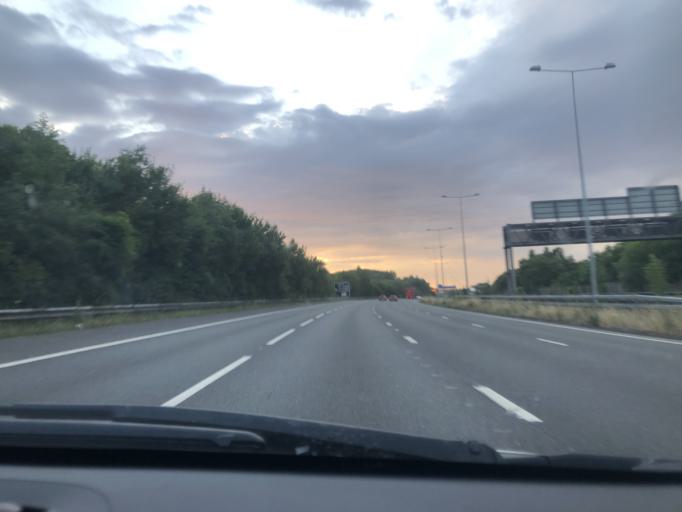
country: GB
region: England
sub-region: Medway
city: Cuxton
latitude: 51.3928
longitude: 0.4577
